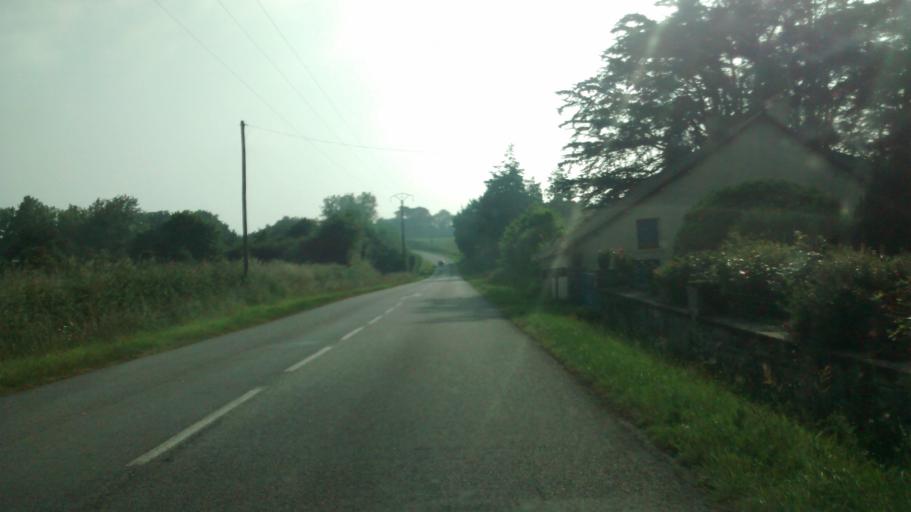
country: FR
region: Brittany
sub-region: Departement du Morbihan
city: Ruffiac
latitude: 47.8647
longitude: -2.2280
